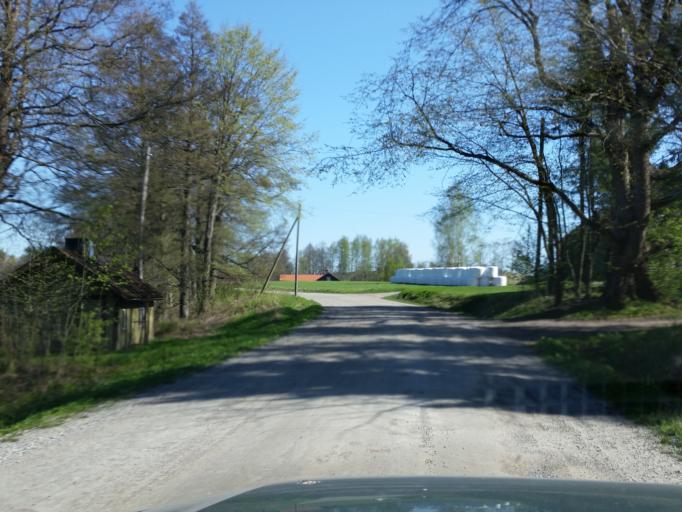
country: FI
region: Uusimaa
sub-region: Helsinki
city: Karjalohja
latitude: 60.1813
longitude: 23.6382
